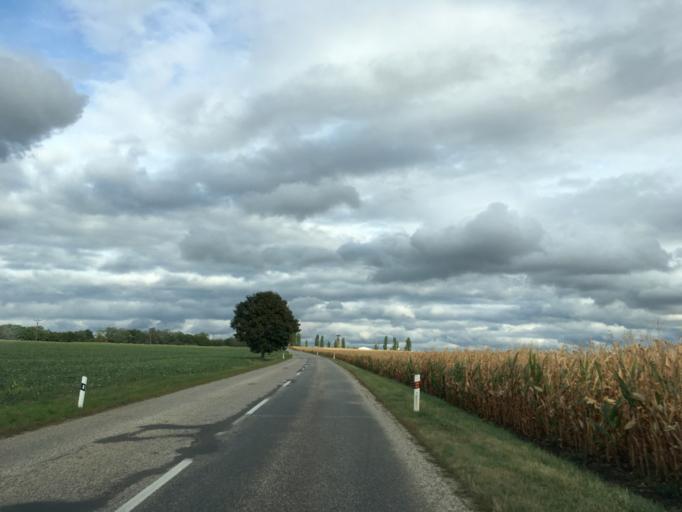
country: SK
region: Nitriansky
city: Svodin
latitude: 47.9826
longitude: 18.3762
